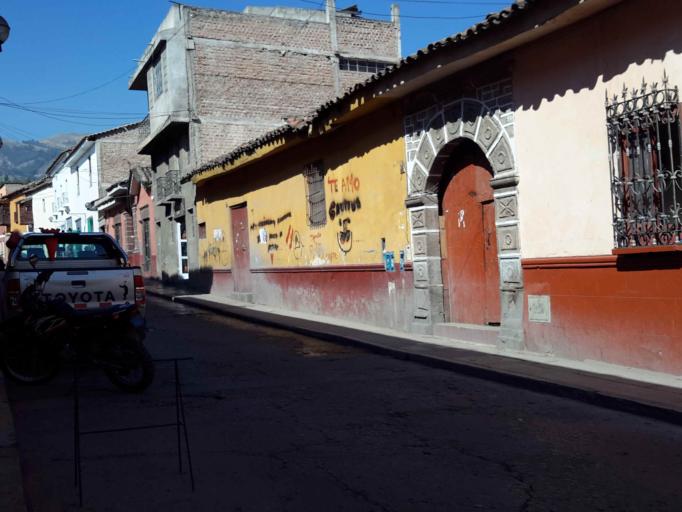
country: PE
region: Ayacucho
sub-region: Provincia de Huamanga
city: Ayacucho
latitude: -13.1659
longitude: -74.2276
